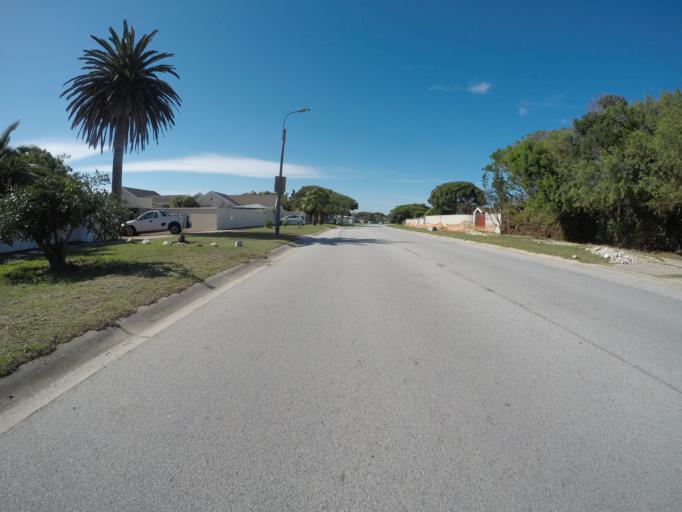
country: ZA
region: Eastern Cape
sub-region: Nelson Mandela Bay Metropolitan Municipality
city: Port Elizabeth
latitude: -33.9926
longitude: 25.6602
